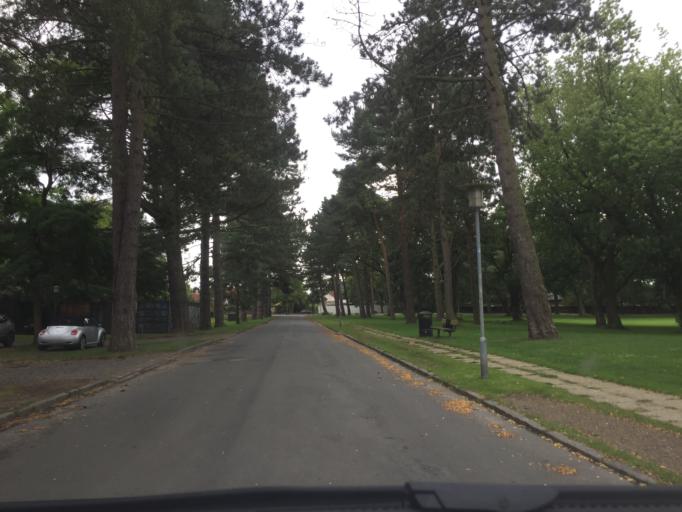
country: DK
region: Capital Region
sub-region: Lyngby-Tarbaek Kommune
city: Kongens Lyngby
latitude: 55.7801
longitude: 12.5071
